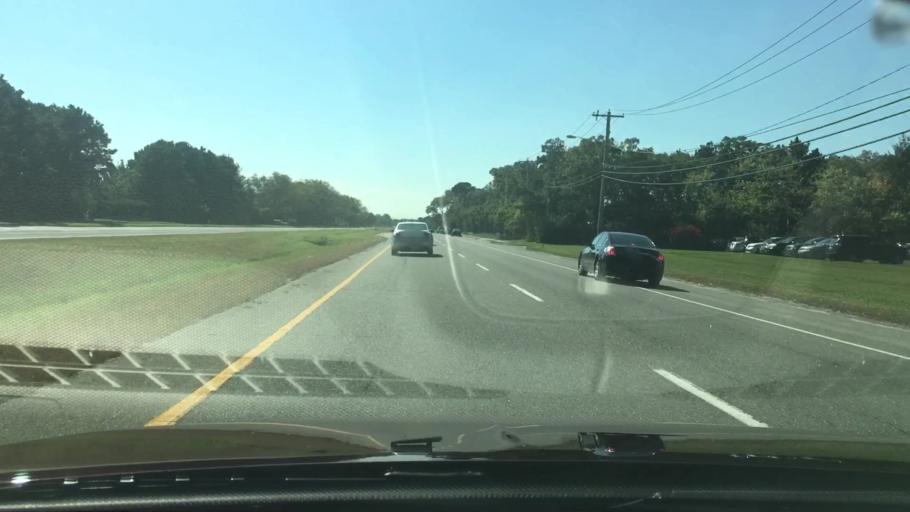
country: US
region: New York
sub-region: Suffolk County
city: Yaphank
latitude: 40.8178
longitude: -72.9481
